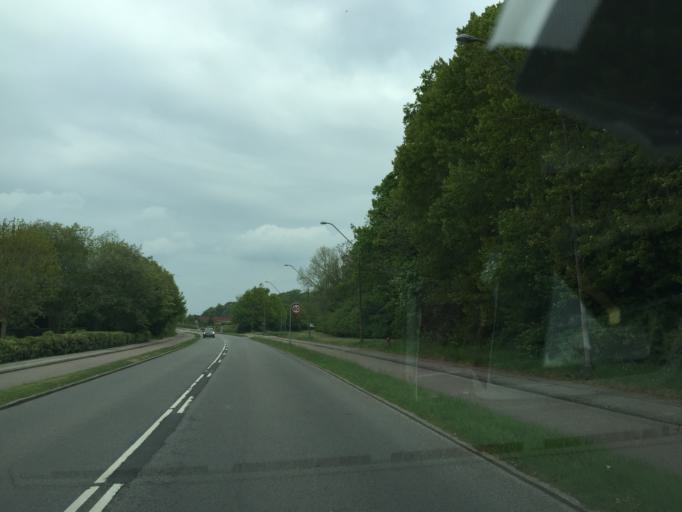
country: DK
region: South Denmark
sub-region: Sonderborg Kommune
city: Sonderborg
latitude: 54.9009
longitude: 9.8242
